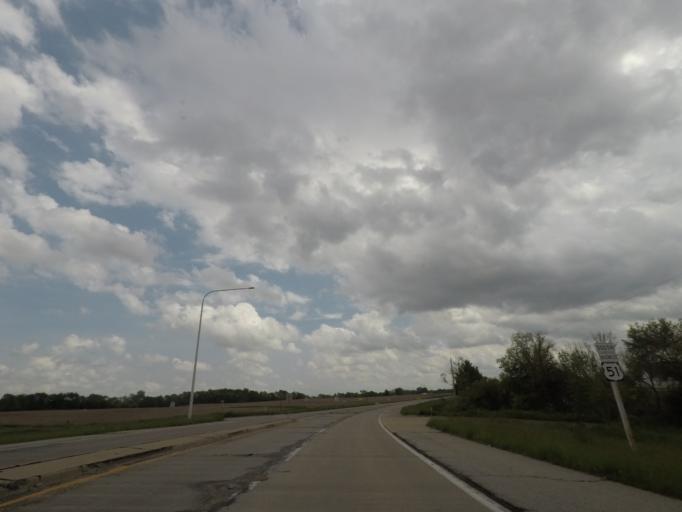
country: US
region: Illinois
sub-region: De Witt County
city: Clinton
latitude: 40.1734
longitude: -88.9613
